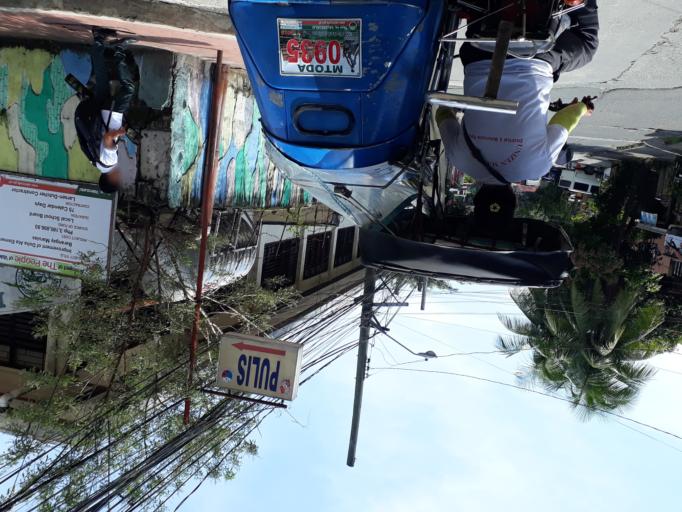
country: PH
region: Calabarzon
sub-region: Province of Rizal
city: Valenzuela
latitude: 14.6779
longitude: 120.9848
